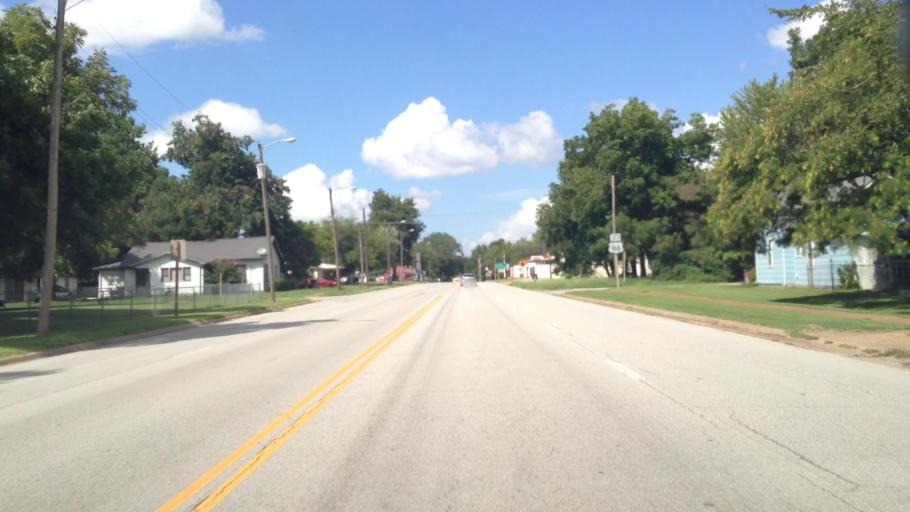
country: US
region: Kansas
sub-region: Labette County
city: Chetopa
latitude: 37.0347
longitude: -95.0861
